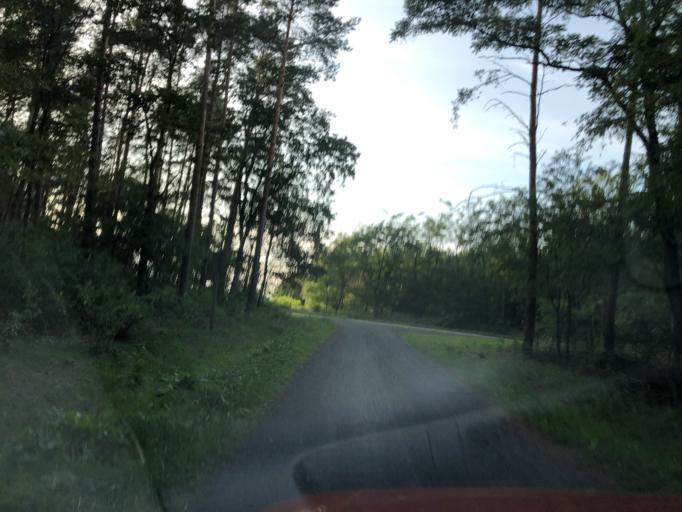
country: PL
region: Lubusz
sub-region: Powiat swiebodzinski
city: Zbaszynek
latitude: 52.2351
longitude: 15.7900
